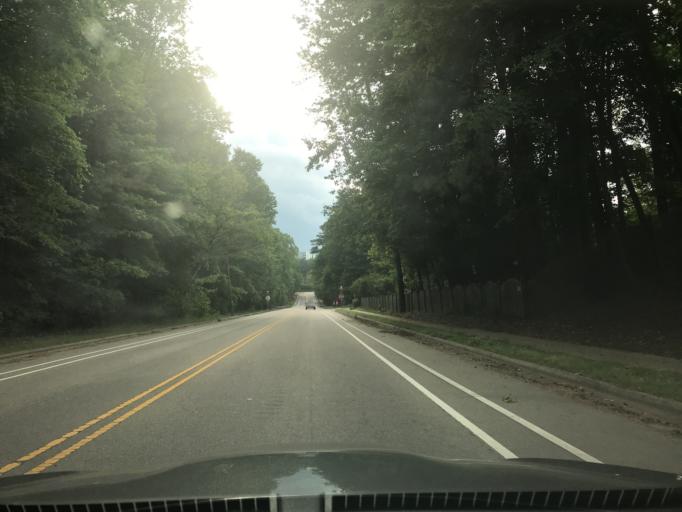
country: US
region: North Carolina
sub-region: Wake County
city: West Raleigh
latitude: 35.8344
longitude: -78.6280
